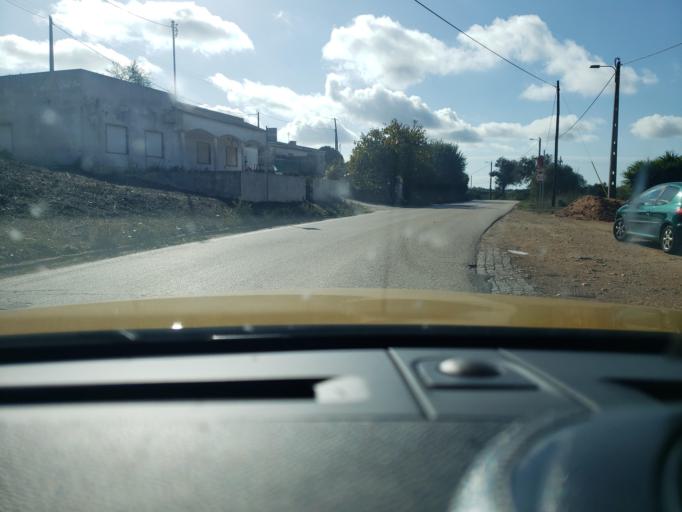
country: PT
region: Faro
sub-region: Portimao
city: Alvor
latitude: 37.1754
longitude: -8.5786
